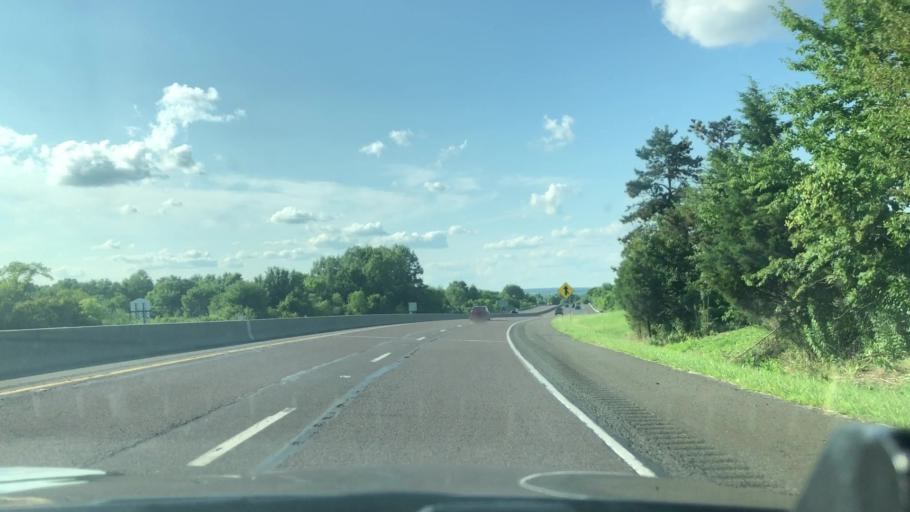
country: US
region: Pennsylvania
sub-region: Montgomery County
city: Souderton
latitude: 40.3183
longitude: -75.3089
